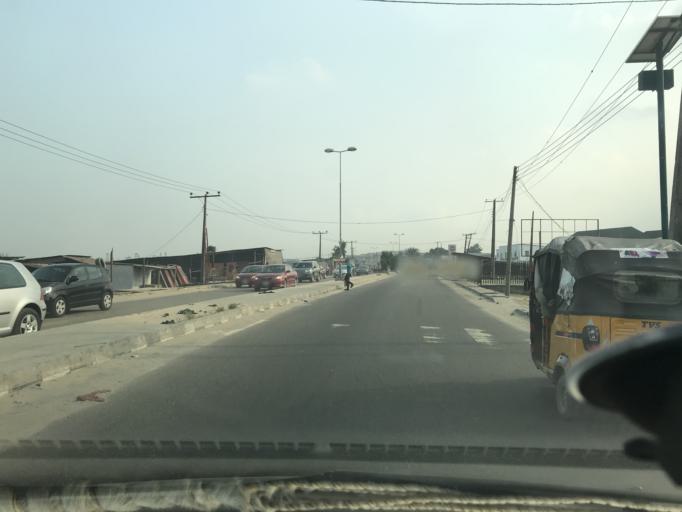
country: NG
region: Lagos
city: Ikoyi
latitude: 6.4777
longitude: 3.5687
